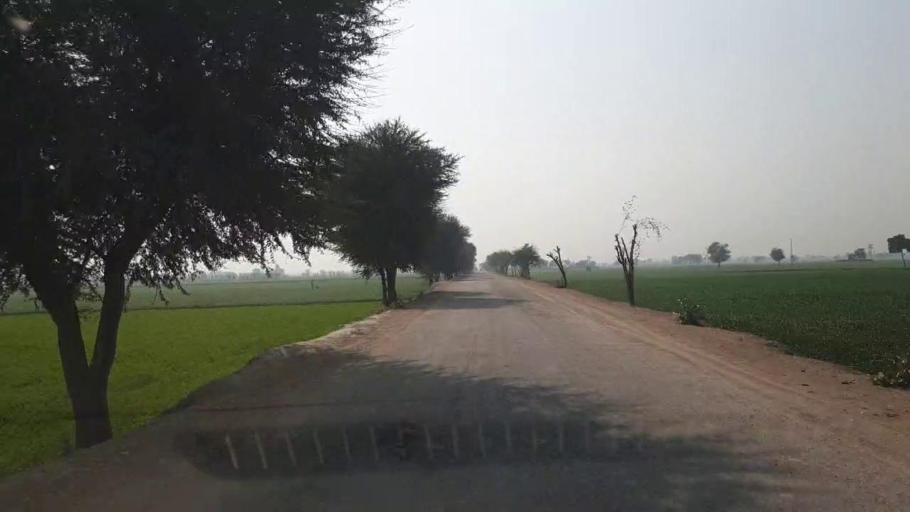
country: PK
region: Sindh
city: Hala
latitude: 25.8833
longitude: 68.4368
